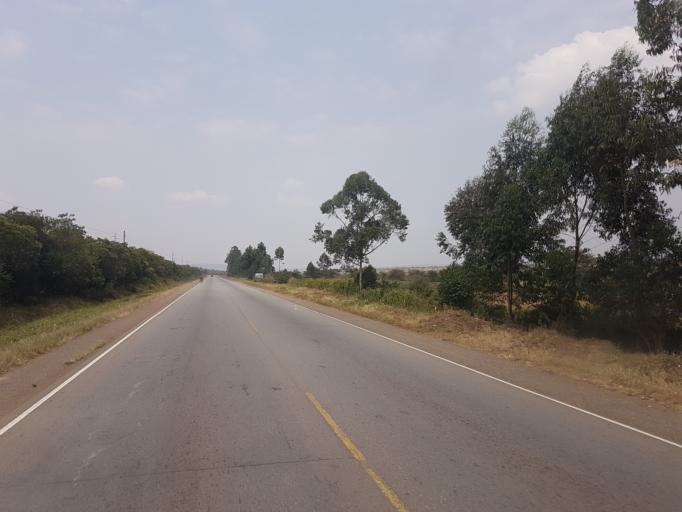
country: UG
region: Western Region
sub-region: Mbarara District
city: Mbarara
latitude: -0.5105
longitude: 30.7865
